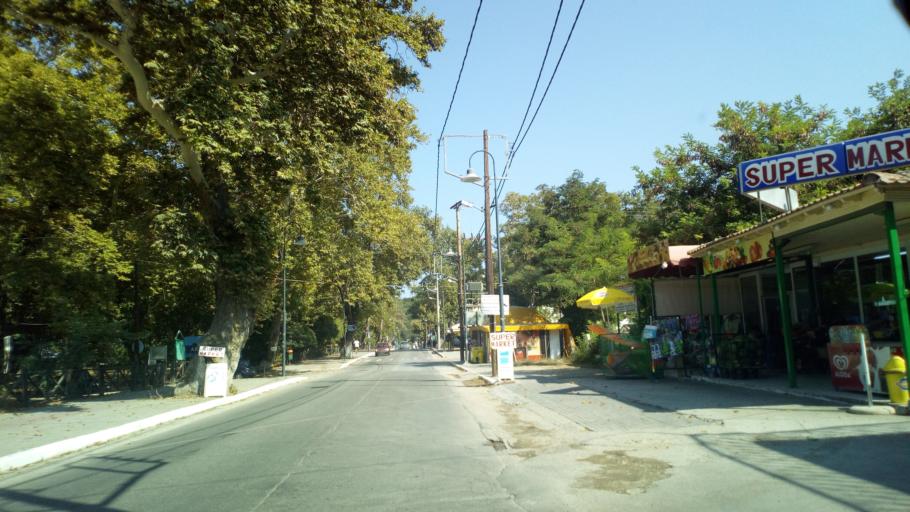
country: GR
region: Central Macedonia
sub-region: Nomos Thessalonikis
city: Stavros
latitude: 40.6635
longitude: 23.7044
